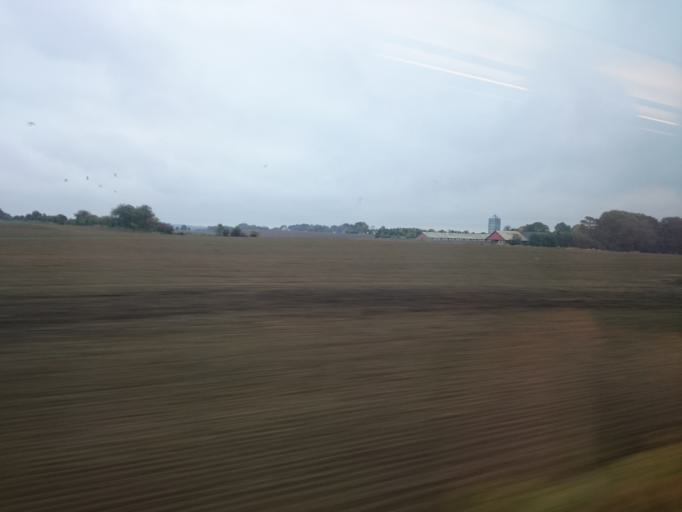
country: DK
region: Central Jutland
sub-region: Arhus Kommune
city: Marslet
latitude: 56.0816
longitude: 10.1527
